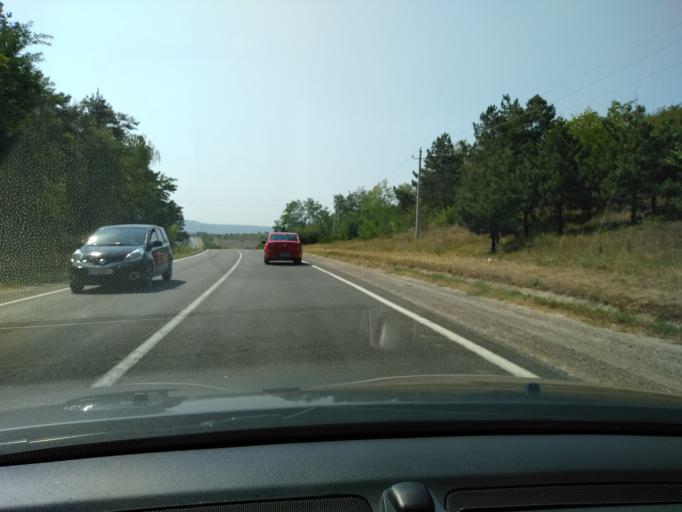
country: MD
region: Chisinau
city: Vatra
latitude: 47.0060
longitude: 28.7078
